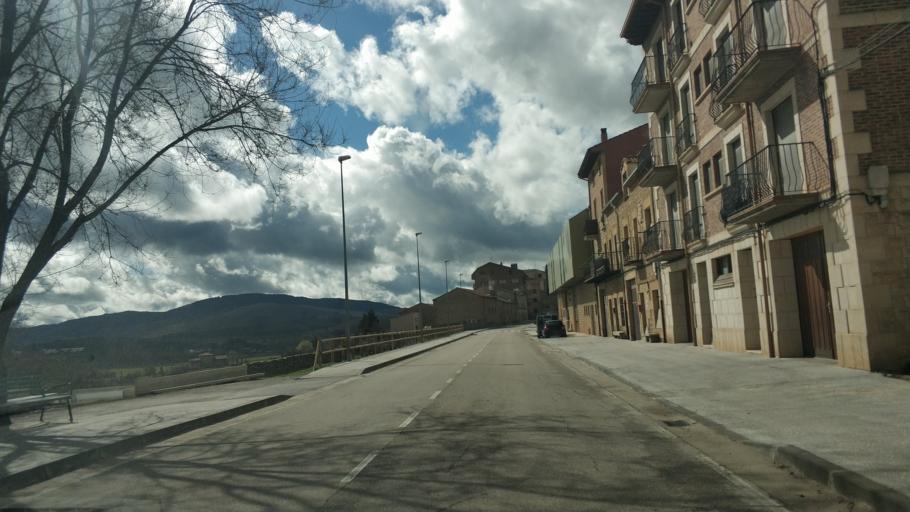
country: ES
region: Castille and Leon
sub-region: Provincia de Burgos
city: Quintanar de la Sierra
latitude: 41.9841
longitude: -3.0345
